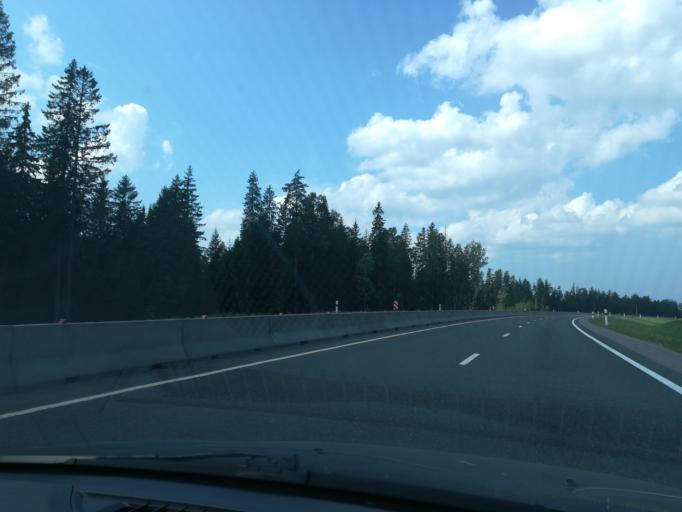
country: RU
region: Leningrad
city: Vistino
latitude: 59.6651
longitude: 28.5237
